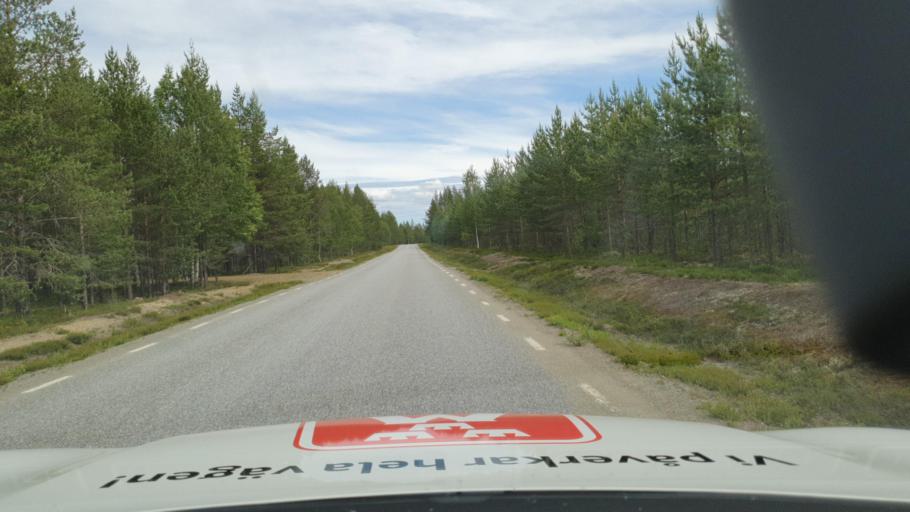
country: SE
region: Vaesterbotten
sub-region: Skelleftea Kommun
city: Burtraesk
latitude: 64.5032
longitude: 20.8271
